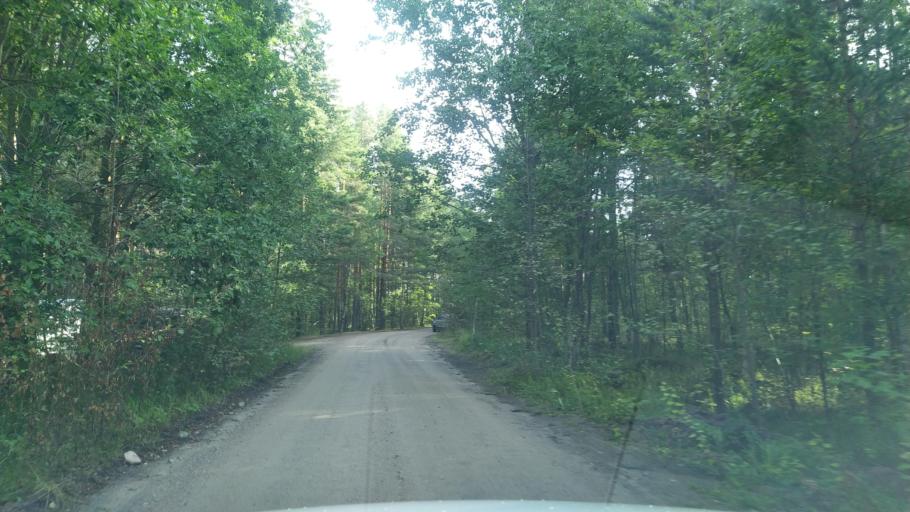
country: RU
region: Leningrad
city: Priozersk
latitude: 60.9723
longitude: 30.3028
